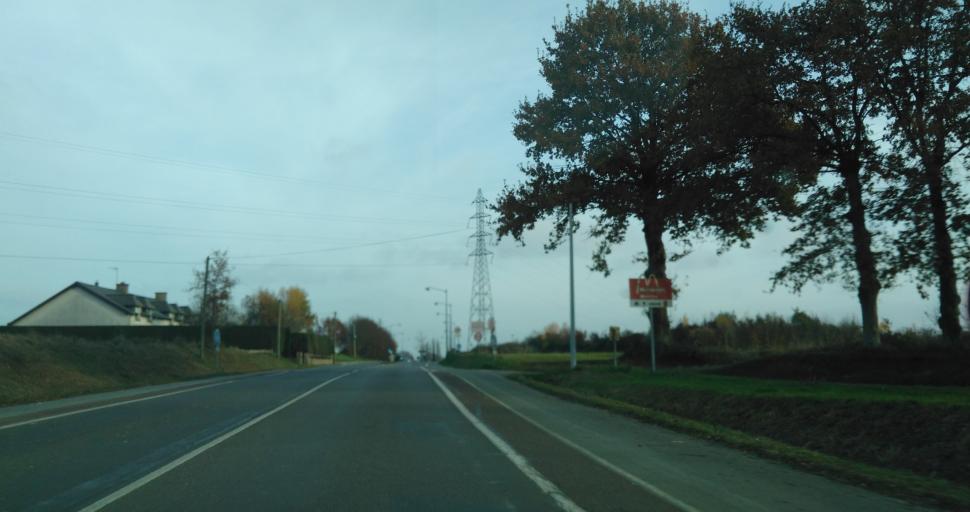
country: FR
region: Brittany
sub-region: Departement d'Ille-et-Vilaine
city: Vezin-le-Coquet
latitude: 48.1173
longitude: -1.7274
